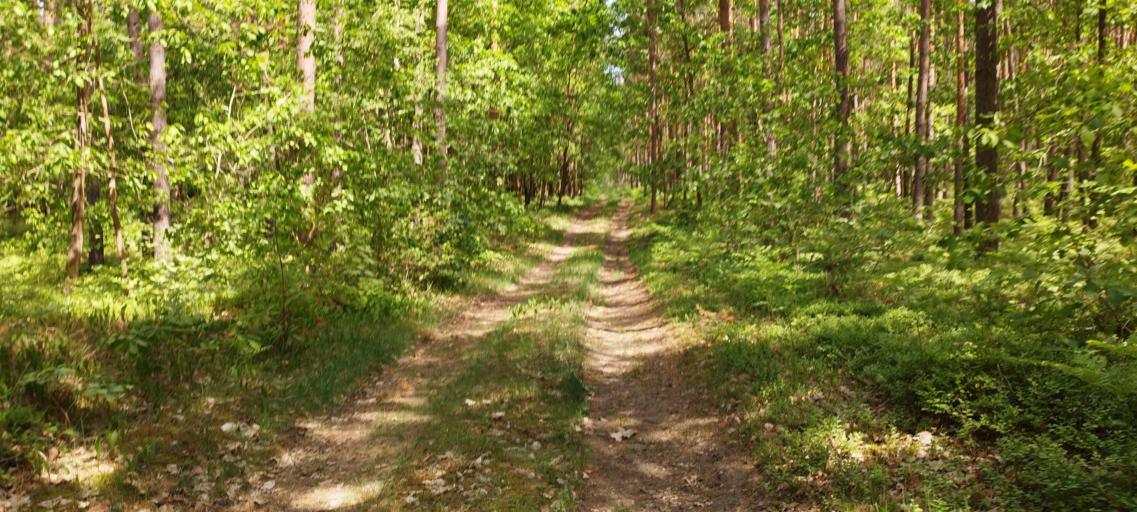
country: DE
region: Brandenburg
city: Spreenhagen
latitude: 52.4006
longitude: 13.9449
